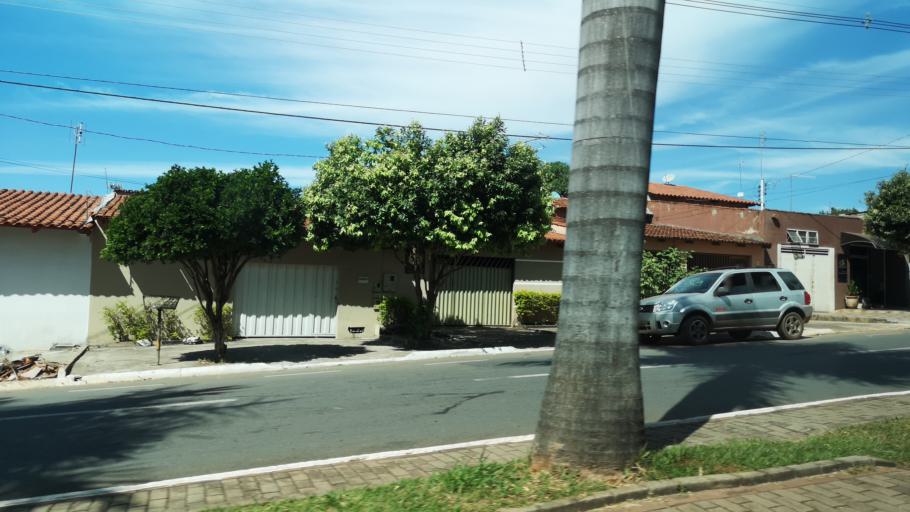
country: BR
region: Goias
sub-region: Senador Canedo
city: Senador Canedo
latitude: -16.6926
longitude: -49.0976
